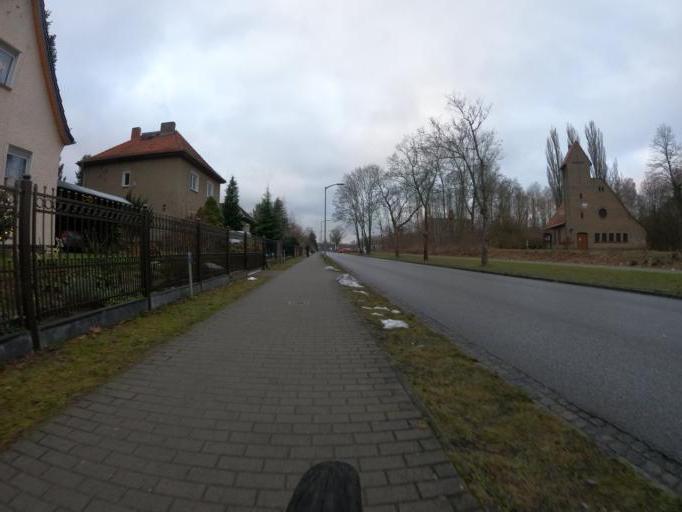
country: DE
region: Brandenburg
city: Schulzendorf
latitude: 52.3643
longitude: 13.5968
